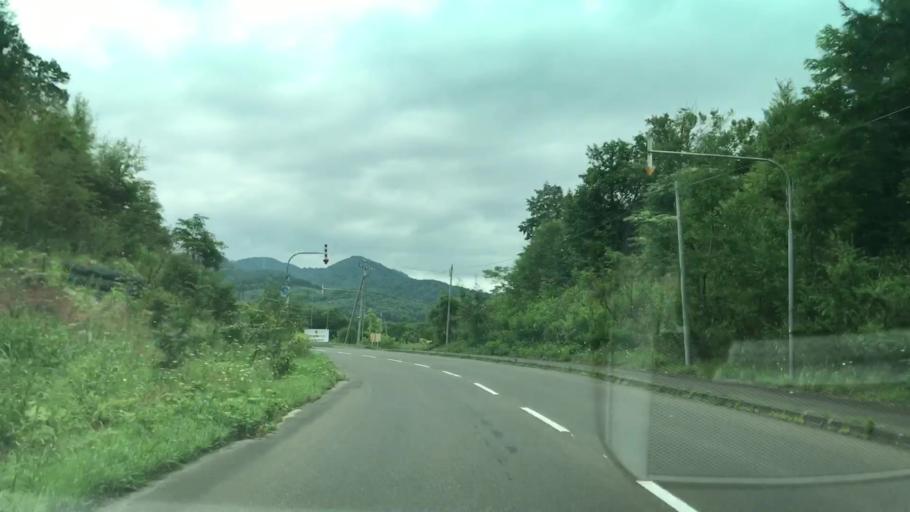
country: JP
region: Hokkaido
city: Yoichi
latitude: 43.0532
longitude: 140.8200
